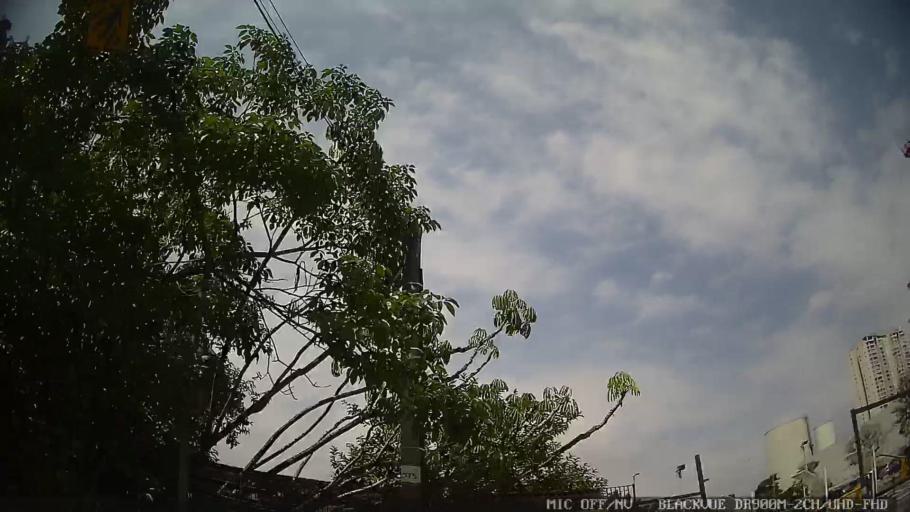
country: BR
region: Sao Paulo
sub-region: Taboao Da Serra
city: Taboao da Serra
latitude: -23.6501
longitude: -46.7214
